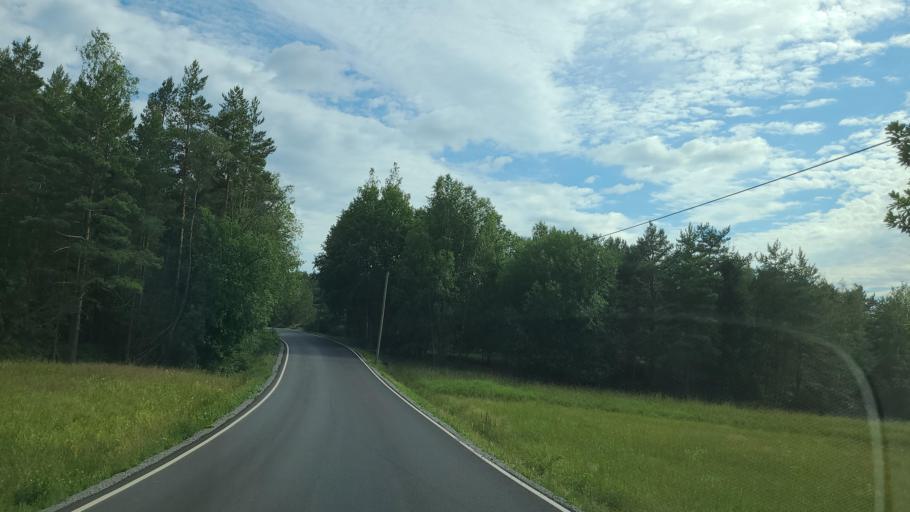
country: FI
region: Varsinais-Suomi
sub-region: Turku
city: Rymaettylae
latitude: 60.3230
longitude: 21.9559
